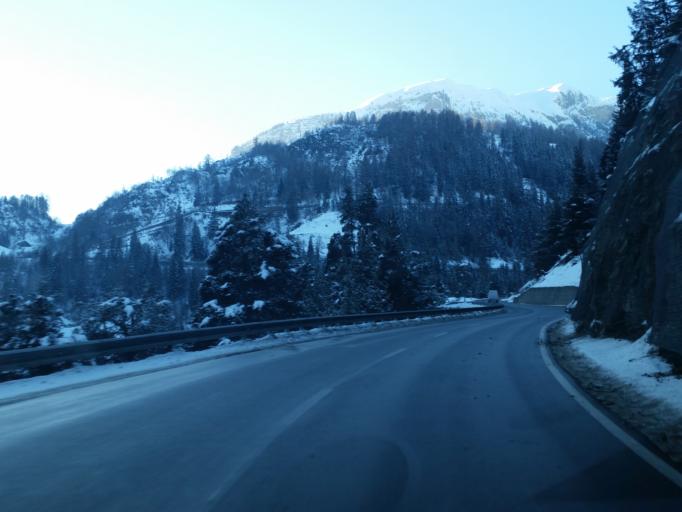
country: CH
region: Grisons
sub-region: Inn District
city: Scuol
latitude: 46.7765
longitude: 10.2302
